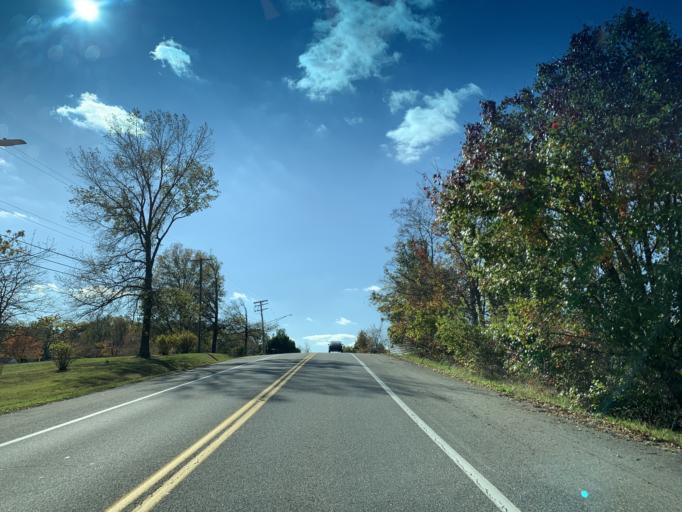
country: US
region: Maryland
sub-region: Anne Arundel County
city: Gambrills
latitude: 39.0787
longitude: -76.6600
